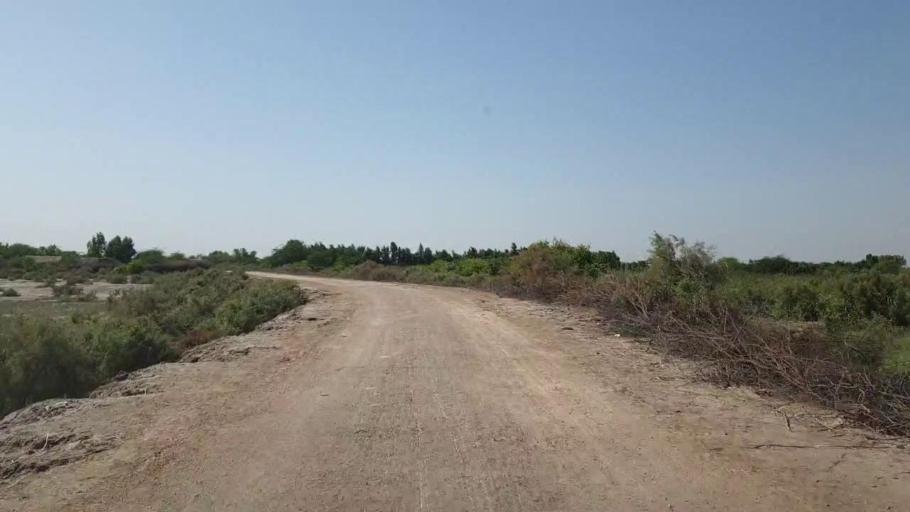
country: PK
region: Sindh
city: Tando Bago
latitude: 24.7054
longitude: 69.0411
